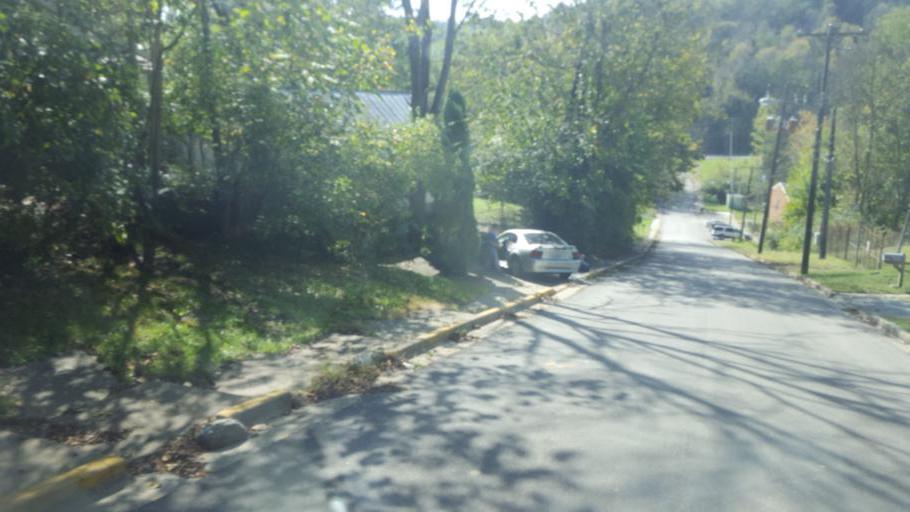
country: US
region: Ohio
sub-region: Brown County
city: Aberdeen
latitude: 38.6413
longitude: -83.7610
